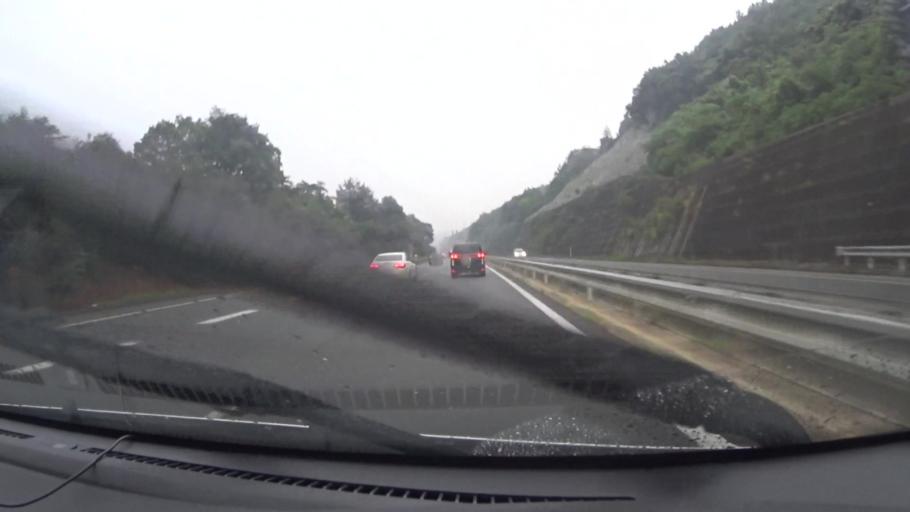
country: JP
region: Kyoto
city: Kameoka
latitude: 35.0055
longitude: 135.5649
